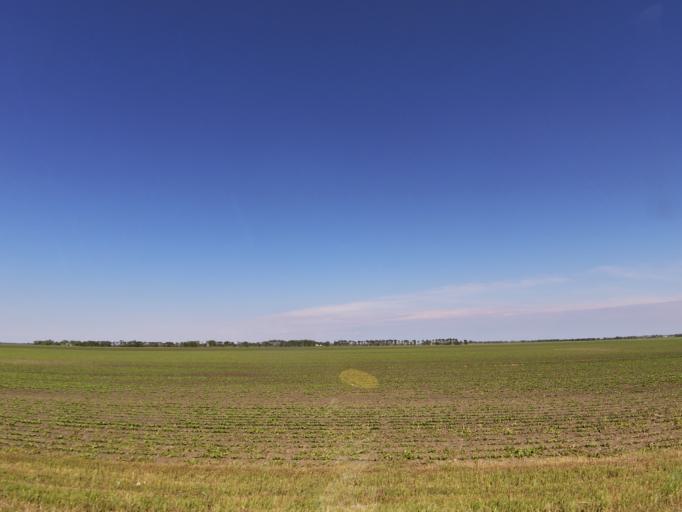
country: US
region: North Dakota
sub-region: Walsh County
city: Grafton
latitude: 48.3409
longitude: -97.2557
